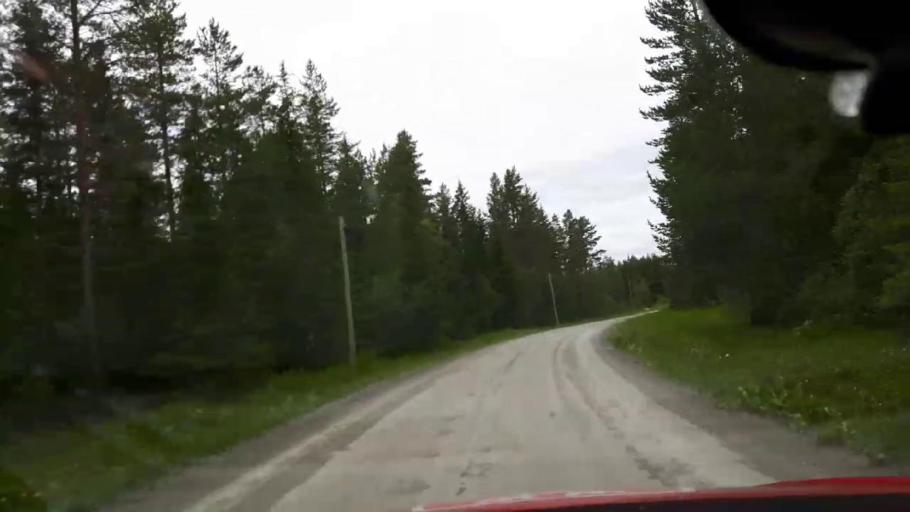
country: SE
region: Jaemtland
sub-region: OEstersunds Kommun
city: Brunflo
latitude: 63.0627
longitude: 14.9045
